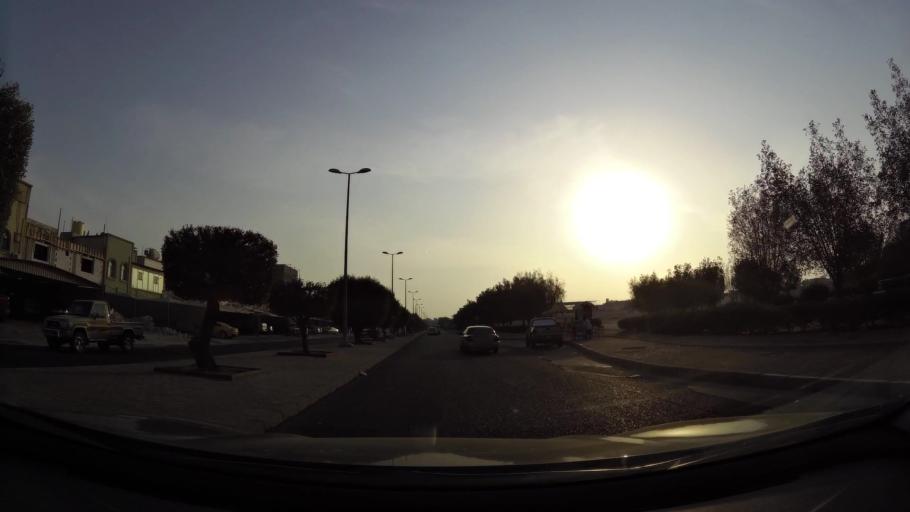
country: KW
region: Mubarak al Kabir
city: Sabah as Salim
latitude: 29.2473
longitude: 48.0647
